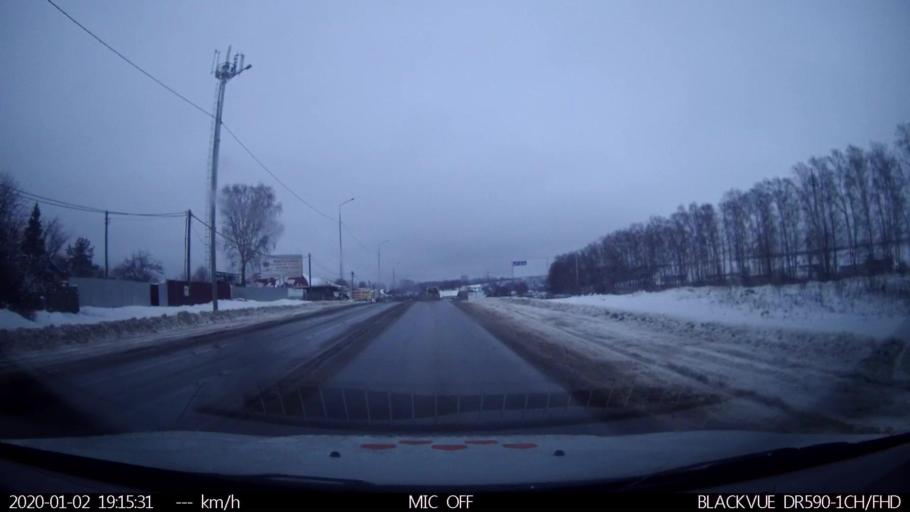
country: RU
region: Nizjnij Novgorod
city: Burevestnik
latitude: 56.2108
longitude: 43.8856
